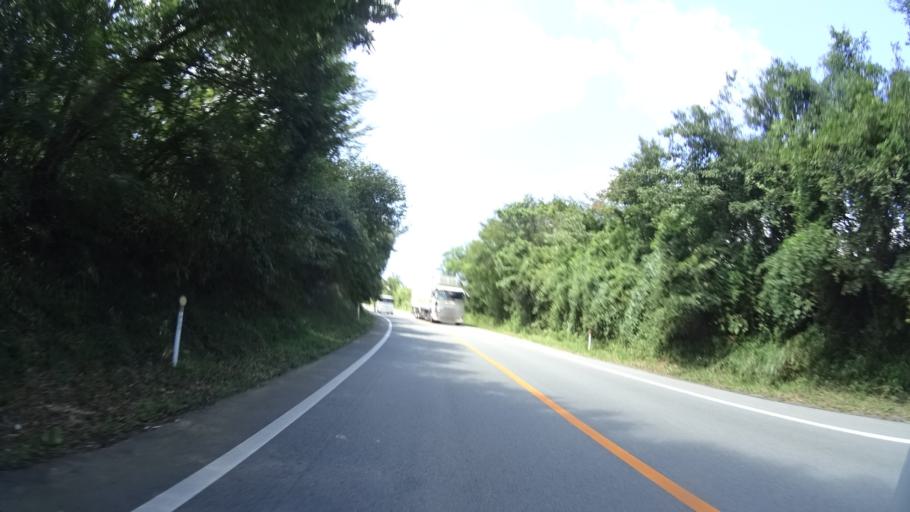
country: JP
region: Kumamoto
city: Aso
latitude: 33.0071
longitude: 131.1001
